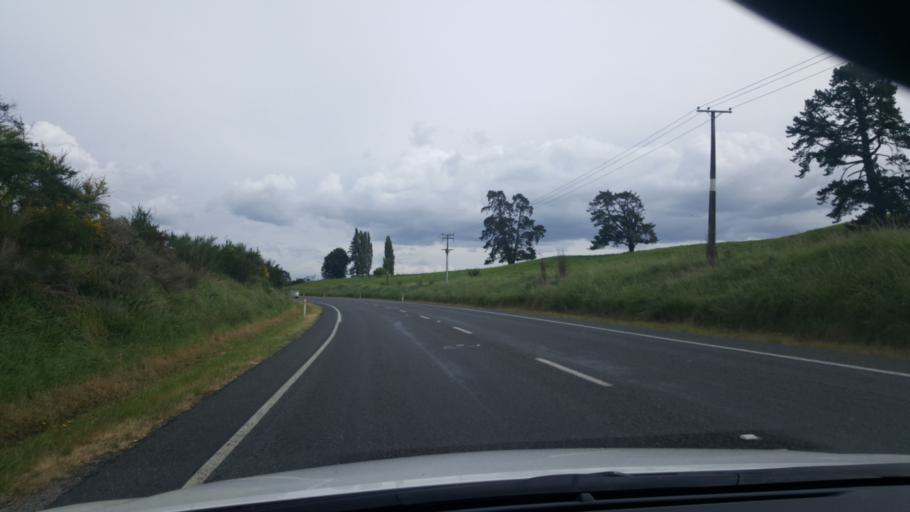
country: NZ
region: Bay of Plenty
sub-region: Rotorua District
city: Rotorua
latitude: -38.4442
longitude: 176.3138
